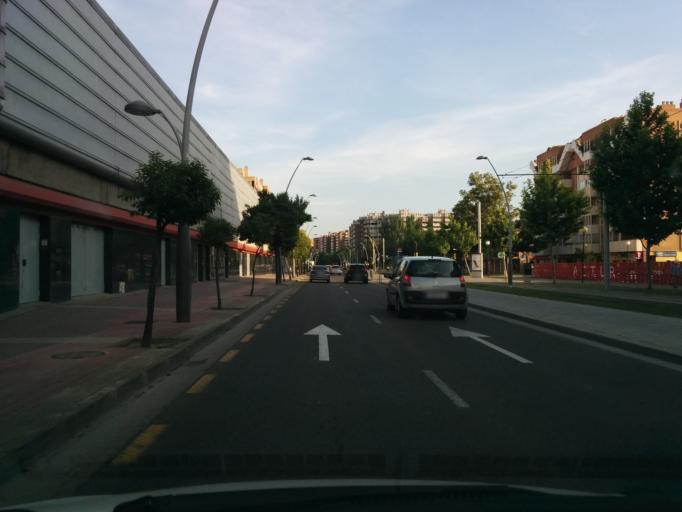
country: ES
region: Aragon
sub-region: Provincia de Zaragoza
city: Almozara
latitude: 41.6759
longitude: -0.8907
